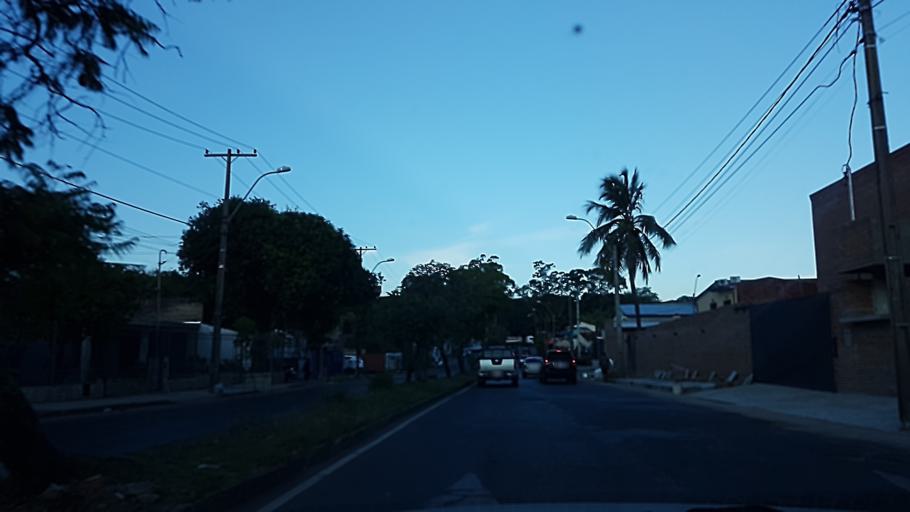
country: PY
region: Asuncion
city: Asuncion
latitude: -25.2552
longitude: -57.5769
